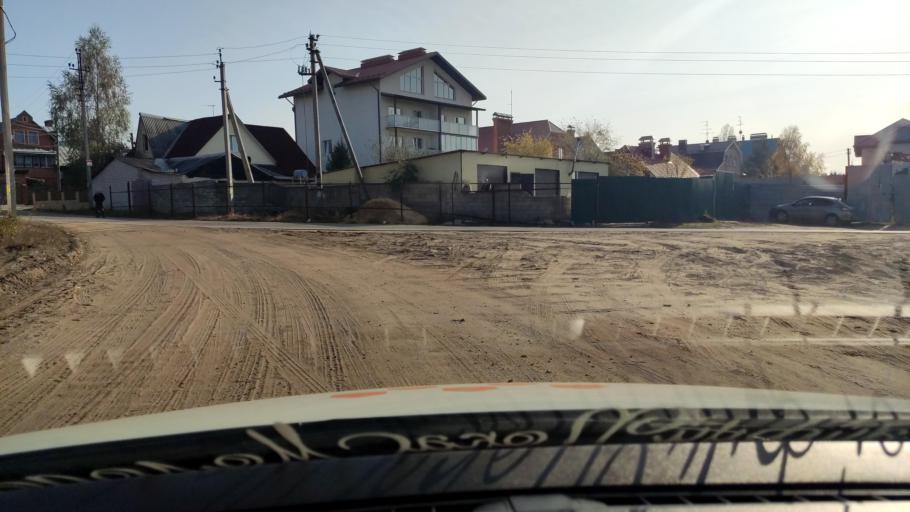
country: RU
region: Voronezj
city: Pridonskoy
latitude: 51.6546
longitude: 39.0954
